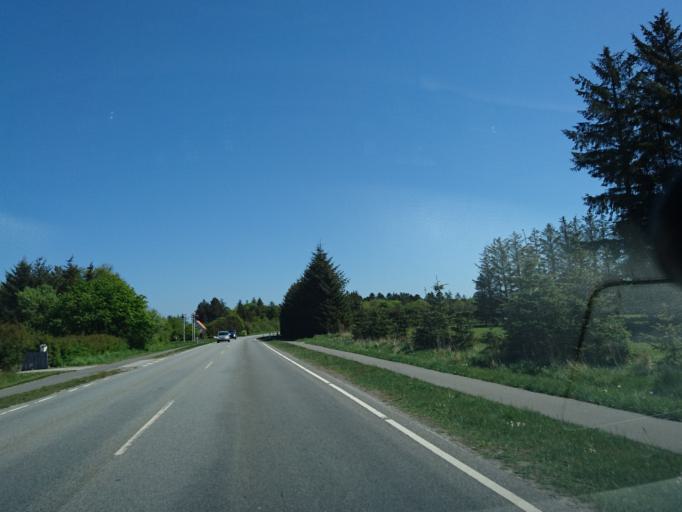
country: DK
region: North Denmark
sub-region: Hjorring Kommune
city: Sindal
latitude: 57.5814
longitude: 10.1977
